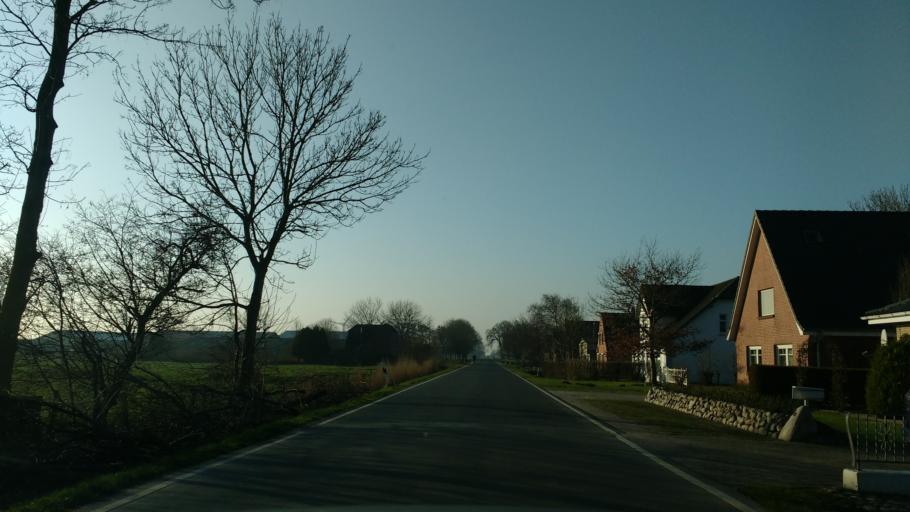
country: DE
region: Schleswig-Holstein
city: Friedrichskoog
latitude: 53.9919
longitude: 8.9408
